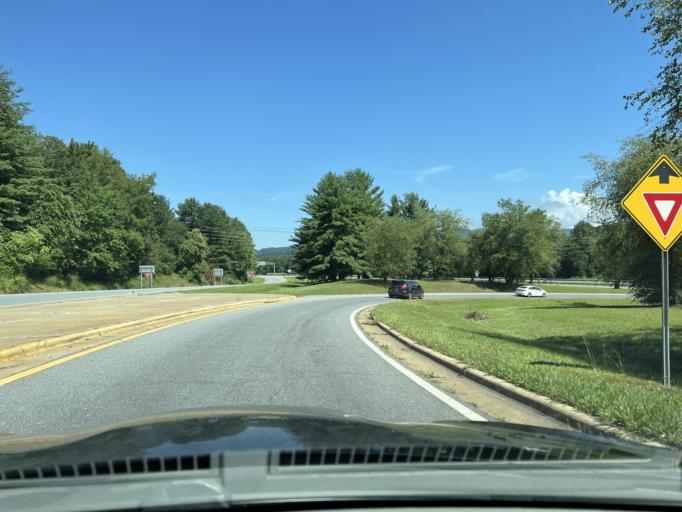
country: US
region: North Carolina
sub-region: Buncombe County
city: Biltmore Forest
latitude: 35.5678
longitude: -82.5097
